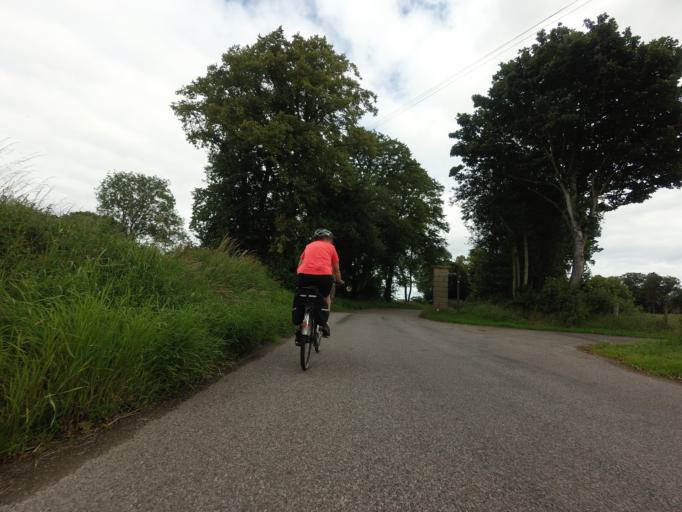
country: GB
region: Scotland
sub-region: Moray
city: Forres
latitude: 57.6169
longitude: -3.6536
